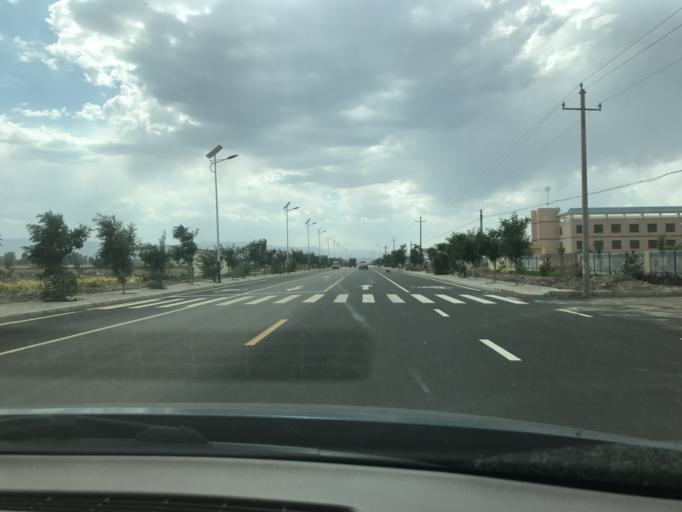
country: CN
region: Gansu Sheng
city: Wuwei
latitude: 38.1031
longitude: 102.4417
